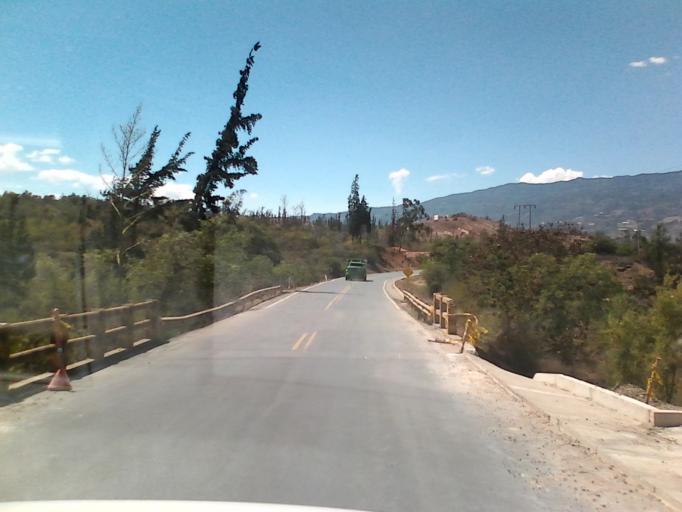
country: CO
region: Boyaca
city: Villa de Leiva
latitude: 5.6231
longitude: -73.5803
